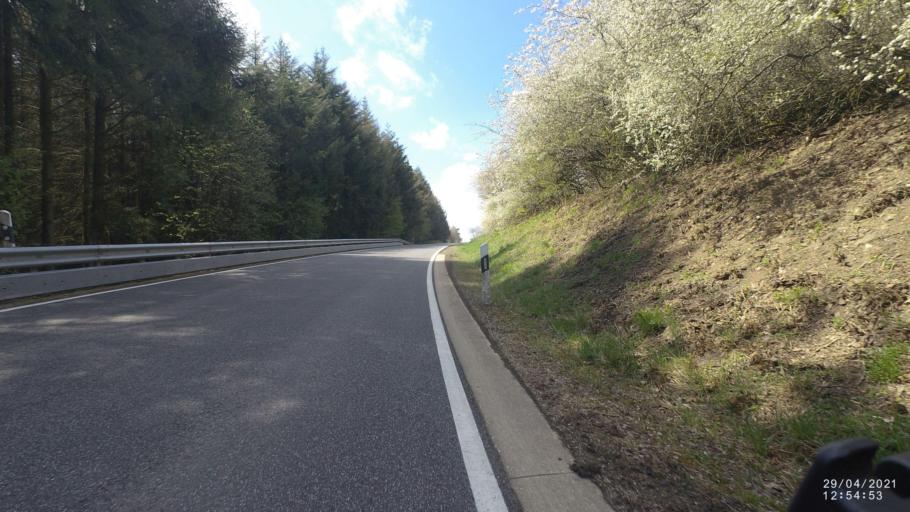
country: DE
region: Rheinland-Pfalz
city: Langscheid
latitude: 50.3696
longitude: 7.1242
